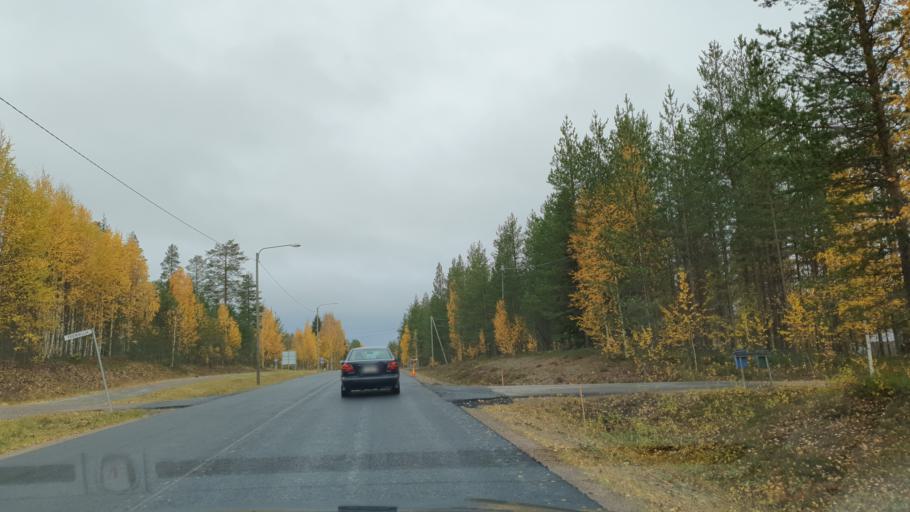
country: FI
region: Lapland
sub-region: Rovaniemi
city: Rovaniemi
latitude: 66.6523
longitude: 25.4514
